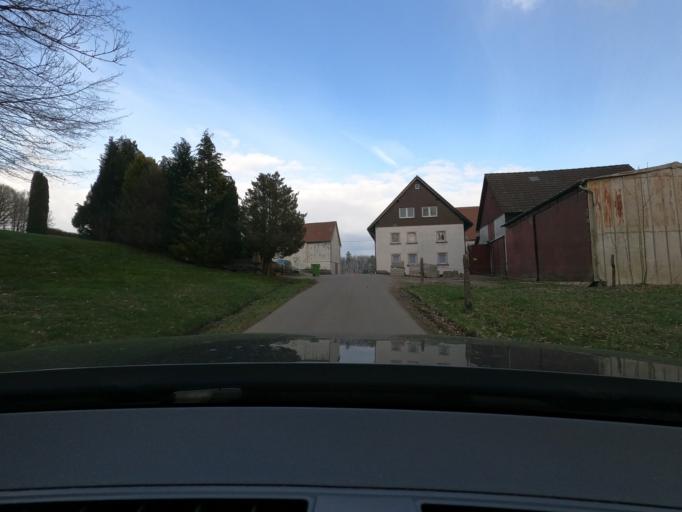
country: DE
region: North Rhine-Westphalia
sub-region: Regierungsbezirk Arnsberg
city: Herscheid
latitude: 51.1159
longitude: 7.7833
